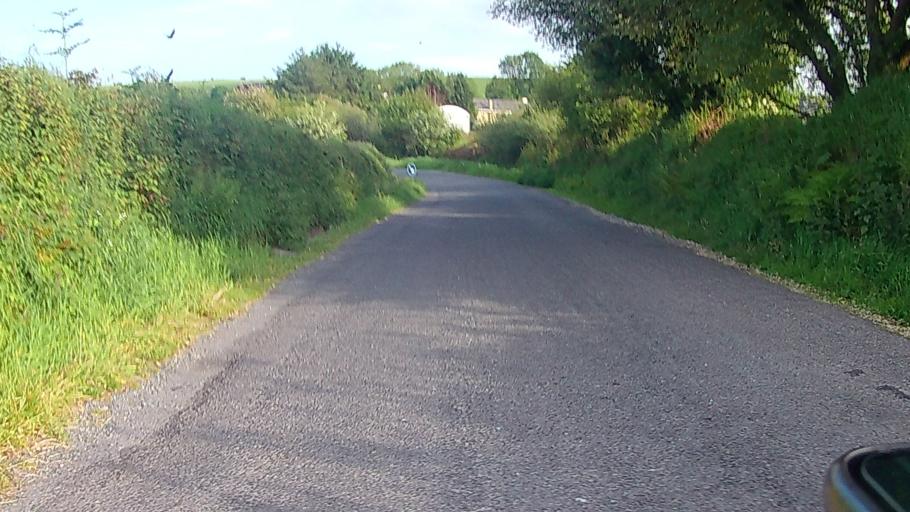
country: IE
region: Munster
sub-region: County Cork
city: Cork
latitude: 51.9747
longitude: -8.4629
